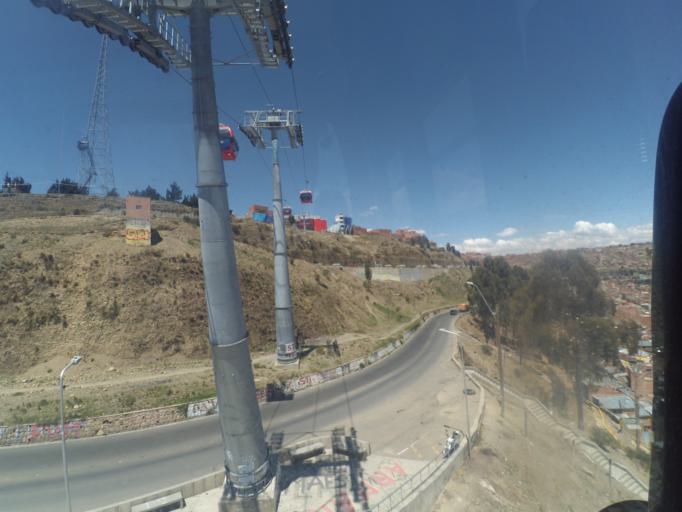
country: BO
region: La Paz
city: La Paz
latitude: -16.4976
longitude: -68.1625
